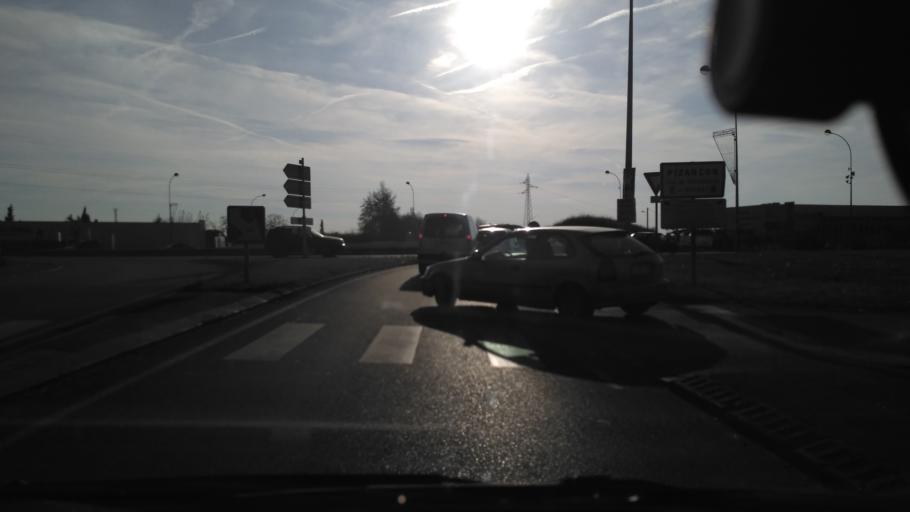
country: FR
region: Rhone-Alpes
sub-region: Departement de la Drome
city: Bourg-de-Peage
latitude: 45.0364
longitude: 5.0826
